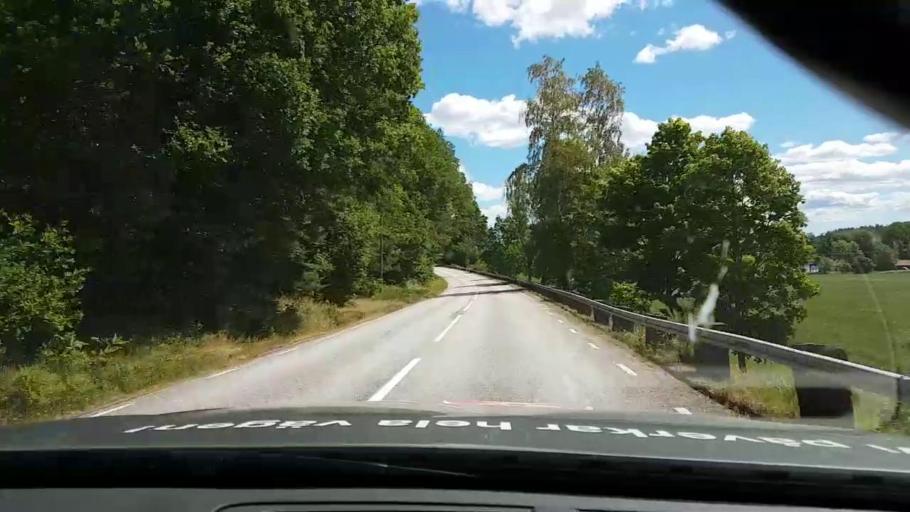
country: SE
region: Kalmar
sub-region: Vasterviks Kommun
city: Overum
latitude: 58.0752
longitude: 16.3630
